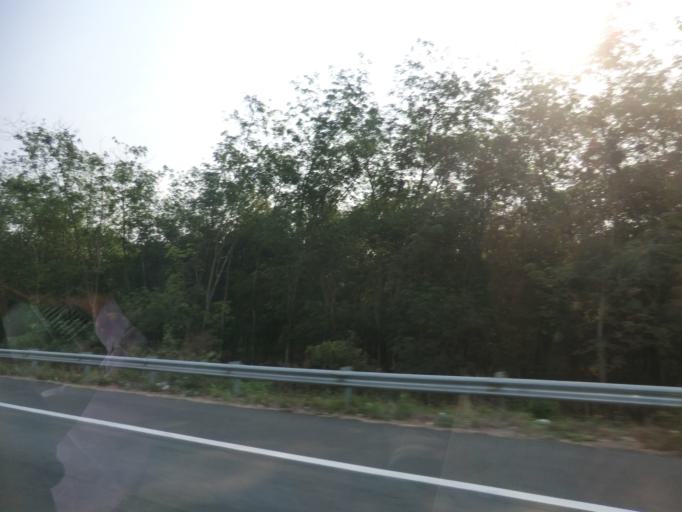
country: VN
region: Dong Nai
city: Thong Nhat
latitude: 10.9231
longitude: 107.1649
